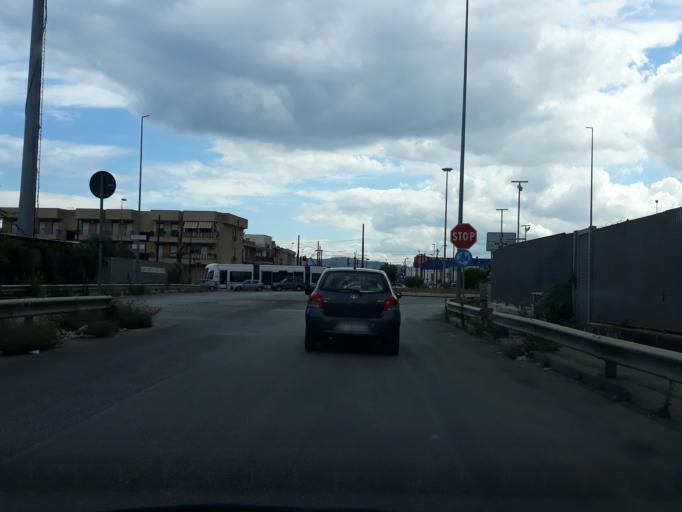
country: IT
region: Sicily
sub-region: Palermo
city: Ciaculli
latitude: 38.0921
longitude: 13.4084
